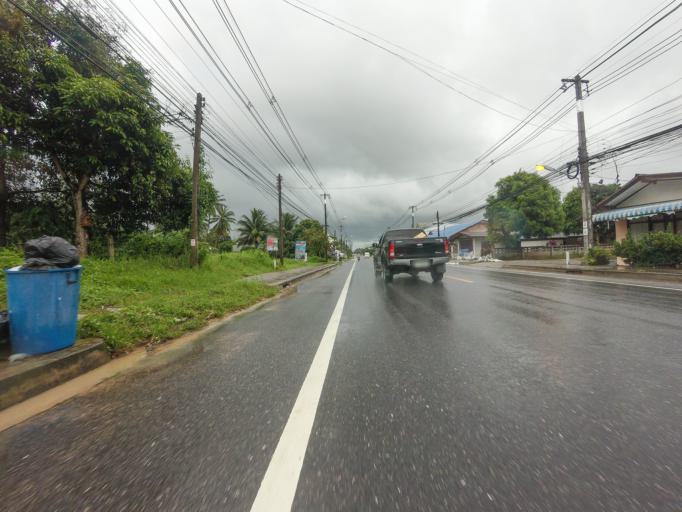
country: TH
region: Surat Thani
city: Ko Samui
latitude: 9.4538
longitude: 99.9963
